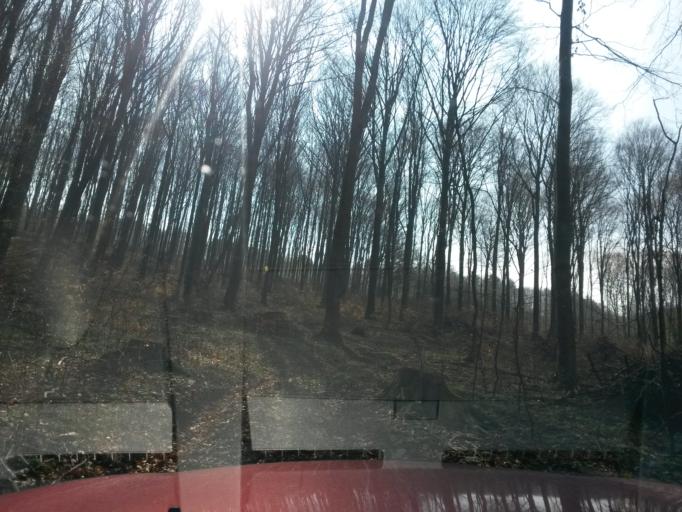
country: SK
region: Presovsky
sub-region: Okres Presov
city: Presov
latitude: 48.9313
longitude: 21.1476
